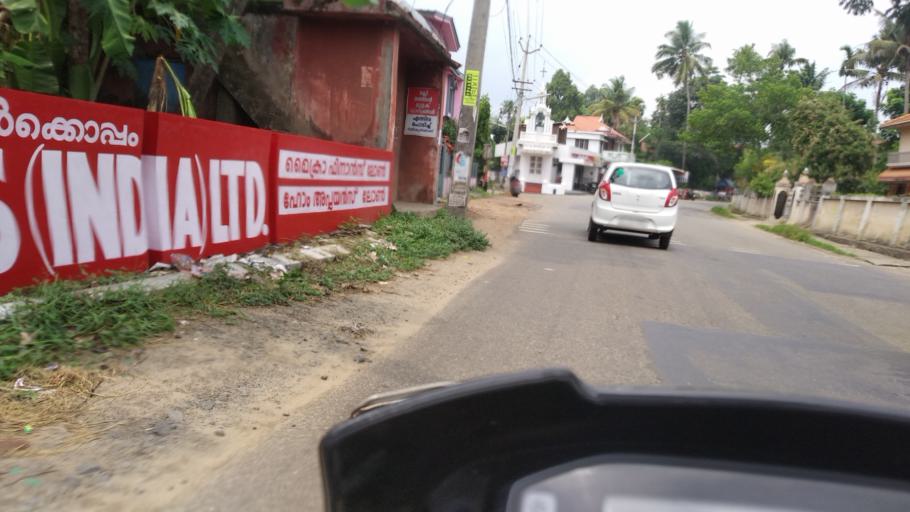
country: IN
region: Kerala
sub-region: Ernakulam
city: Perumpavur
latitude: 10.1114
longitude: 76.5306
